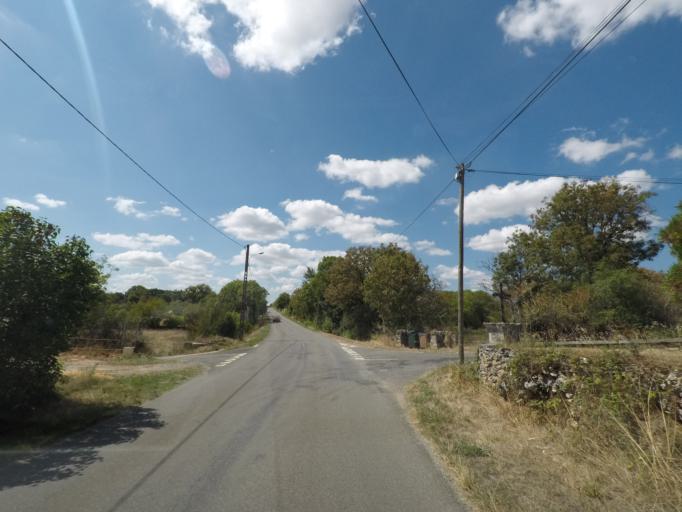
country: FR
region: Midi-Pyrenees
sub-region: Departement du Lot
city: Lacapelle-Marival
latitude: 44.6272
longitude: 1.8241
